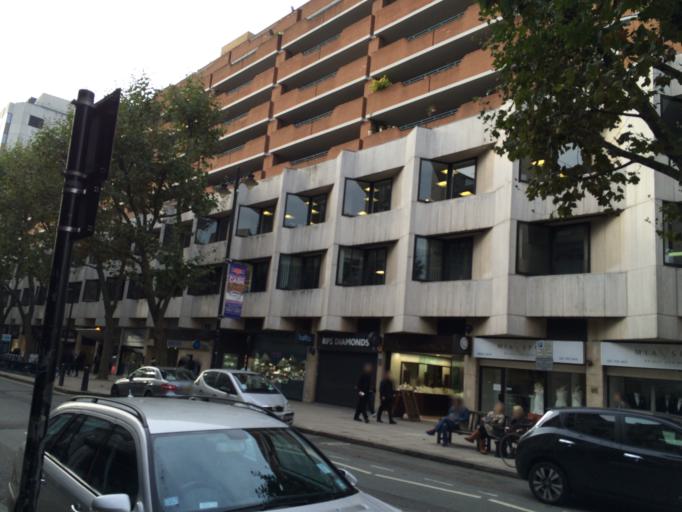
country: GB
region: England
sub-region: Greater London
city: Clerkenwell
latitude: 51.5193
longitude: -0.1083
